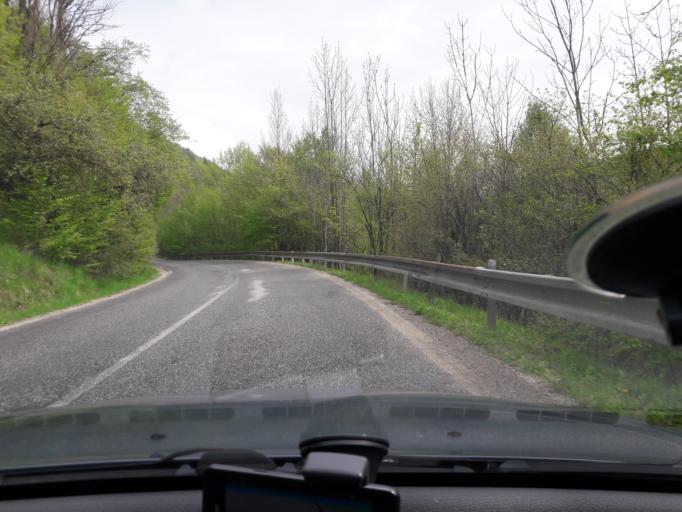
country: SK
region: Banskobystricky
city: Tisovec
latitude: 48.6941
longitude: 19.9733
